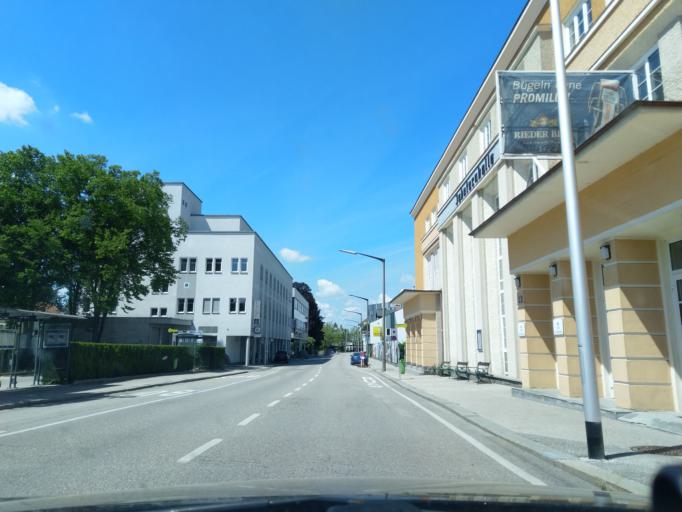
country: AT
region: Upper Austria
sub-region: Politischer Bezirk Ried im Innkreis
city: Ried im Innkreis
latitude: 48.2101
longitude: 13.4859
